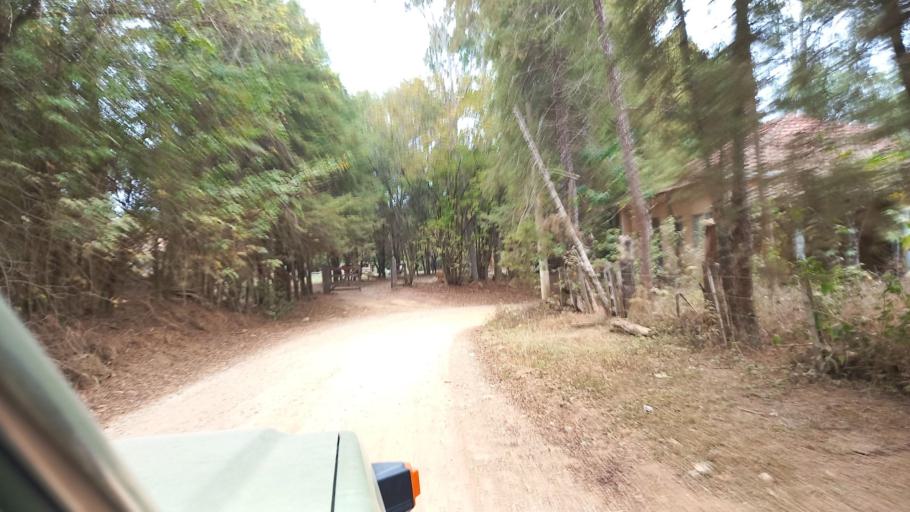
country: BR
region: Sao Paulo
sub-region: Moji-Guacu
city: Mogi-Gaucu
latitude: -22.3086
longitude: -46.8351
